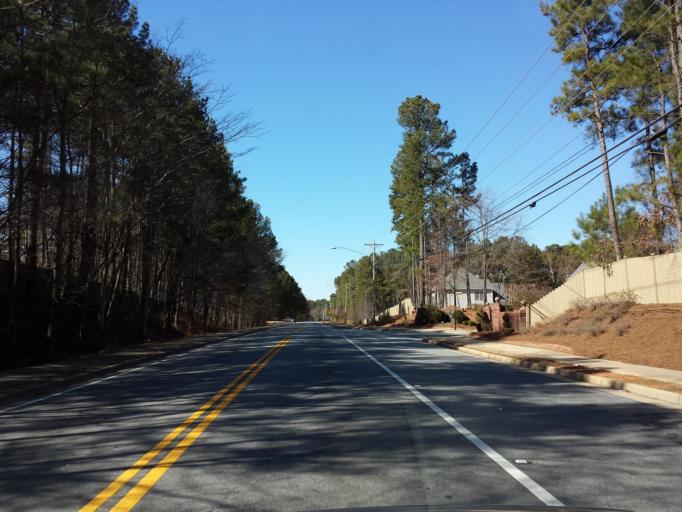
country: US
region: Georgia
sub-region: Cobb County
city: Fair Oaks
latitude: 33.9088
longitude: -84.6070
